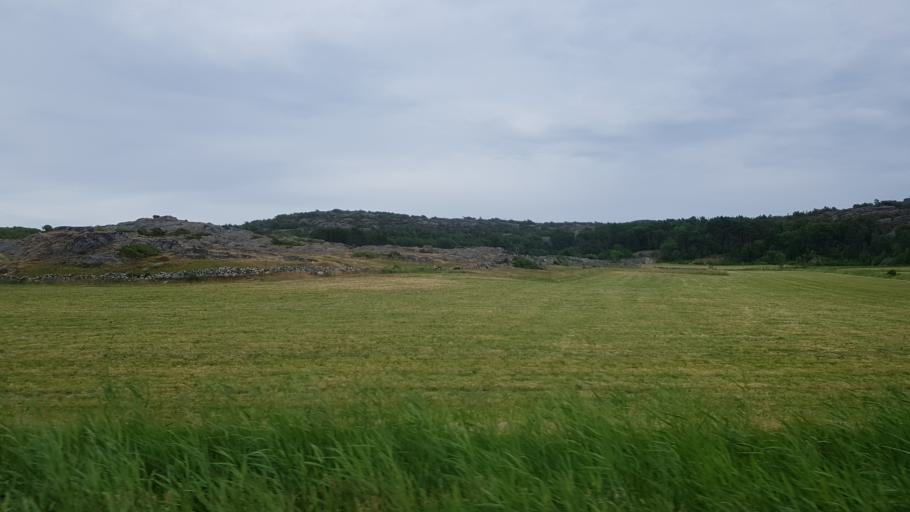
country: SE
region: Vaestra Goetaland
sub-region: Tjorns Kommun
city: Skaerhamn
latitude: 57.9755
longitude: 11.5626
